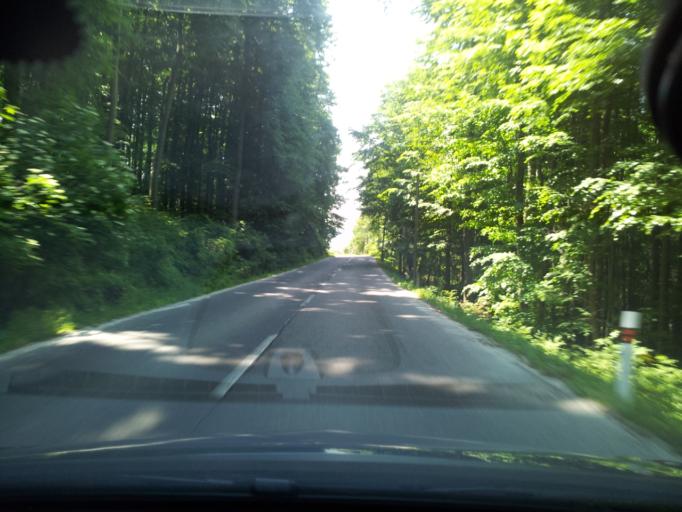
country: SK
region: Nitriansky
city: Partizanske
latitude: 48.5315
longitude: 18.4418
